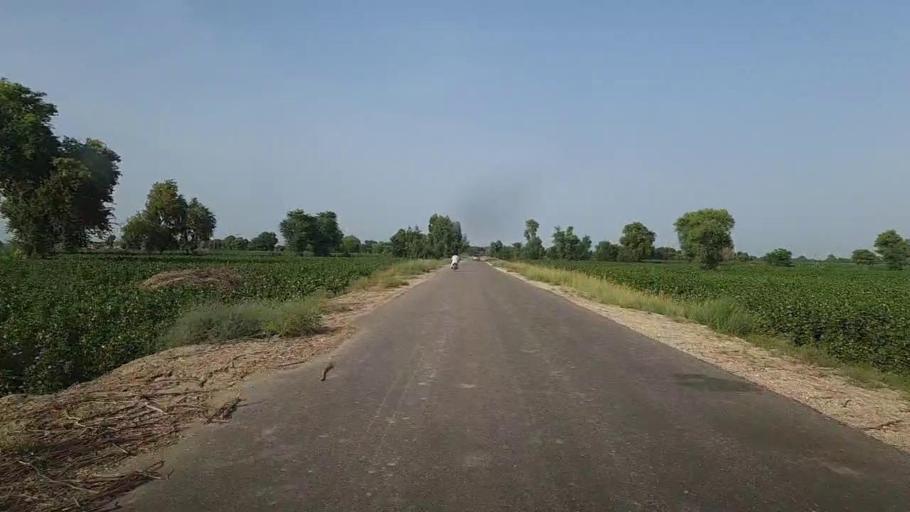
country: PK
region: Sindh
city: Ubauro
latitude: 28.0814
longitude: 69.8353
